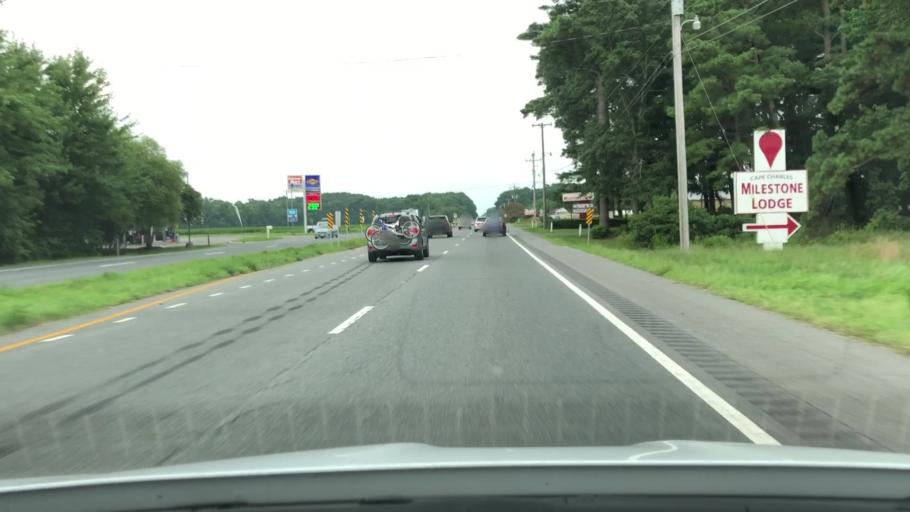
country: US
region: Virginia
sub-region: Northampton County
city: Cape Charles
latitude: 37.2672
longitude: -75.9746
